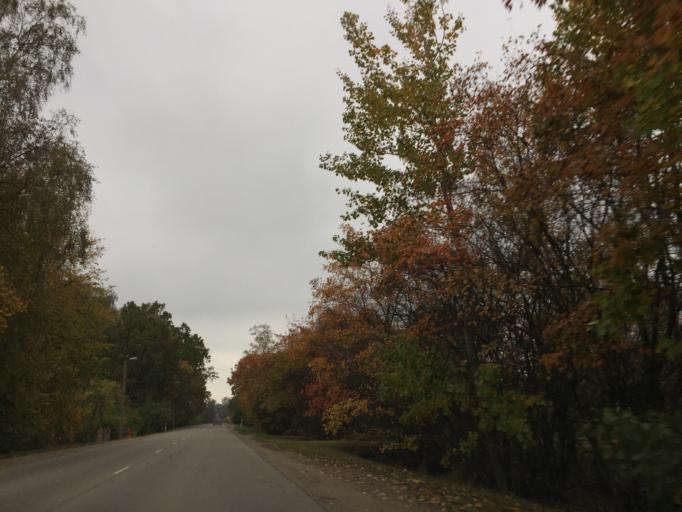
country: LV
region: Jelgava
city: Jelgava
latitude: 56.6623
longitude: 23.7369
